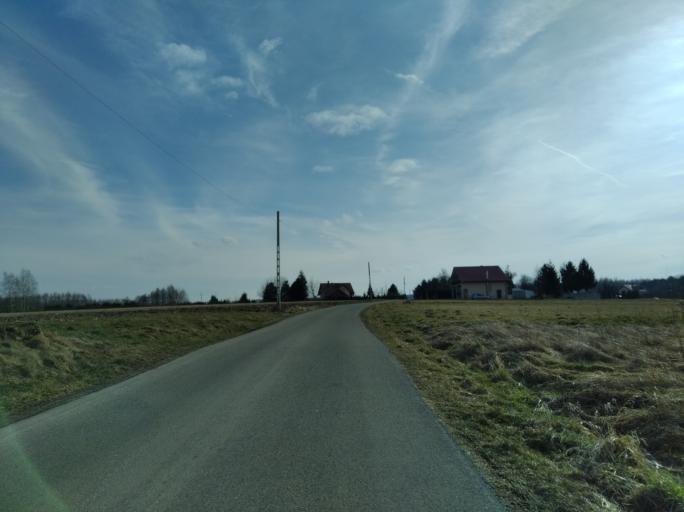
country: PL
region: Subcarpathian Voivodeship
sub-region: Powiat brzozowski
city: Grabownica Starzenska
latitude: 49.6505
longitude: 22.0701
